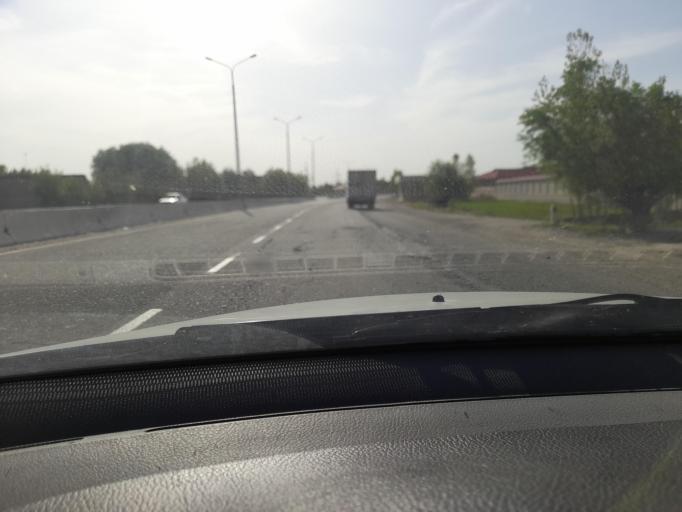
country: UZ
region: Samarqand
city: Kattaqo'rg'on
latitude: 39.9235
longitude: 66.2792
